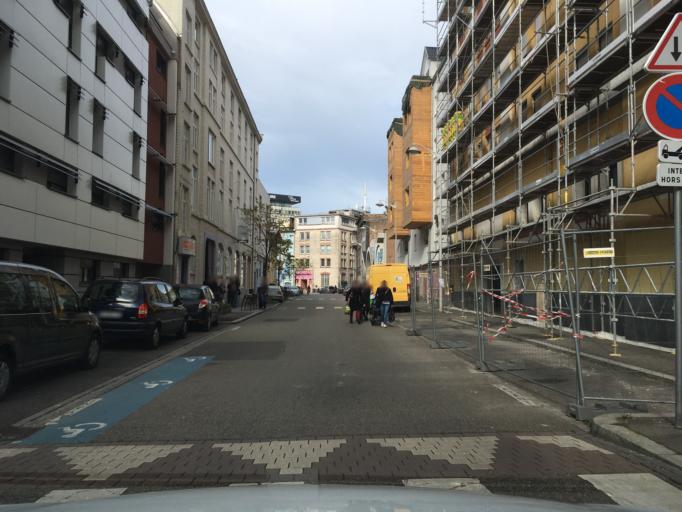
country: FR
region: Alsace
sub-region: Departement du Bas-Rhin
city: Strasbourg
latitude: 48.5900
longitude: 7.7401
